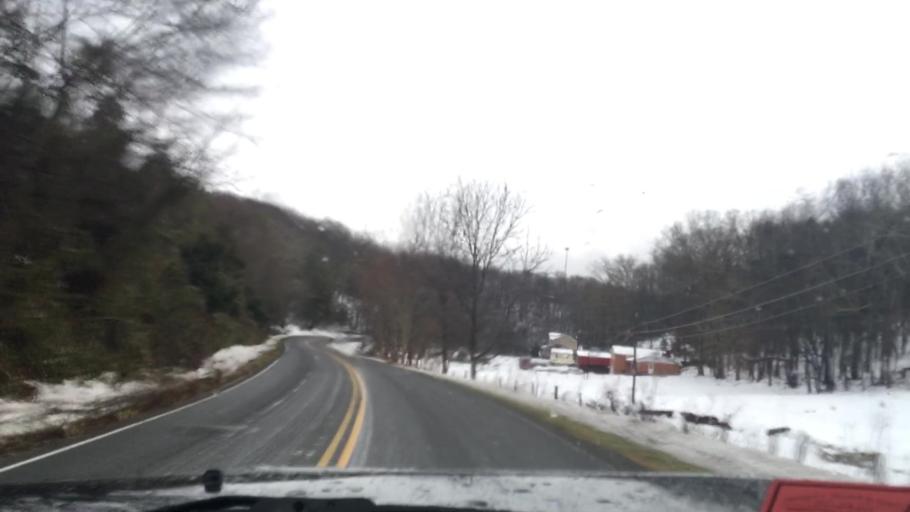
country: US
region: Virginia
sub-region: Pulaski County
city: Dublin
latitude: 37.0109
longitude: -80.6915
